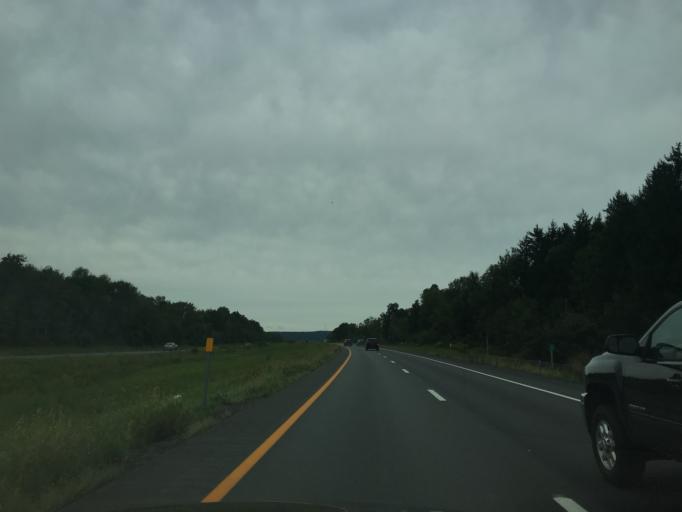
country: US
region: New York
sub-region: Broome County
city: Chenango Bridge
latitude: 42.0761
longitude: -75.8018
